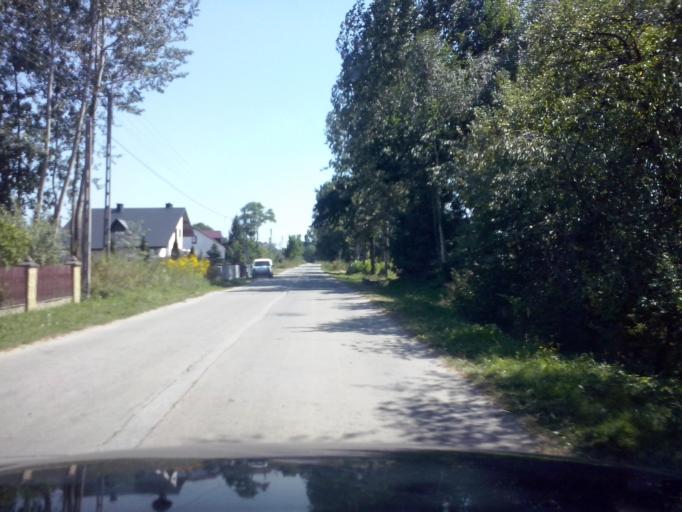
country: PL
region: Swietokrzyskie
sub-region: Powiat buski
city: Gnojno
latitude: 50.6009
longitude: 20.8014
